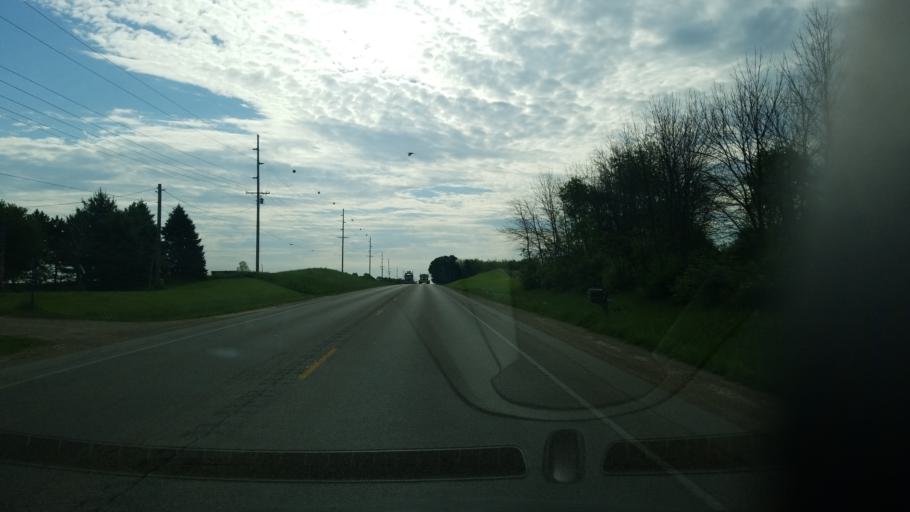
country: US
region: Wisconsin
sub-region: Dane County
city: Oregon
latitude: 42.9182
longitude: -89.3457
